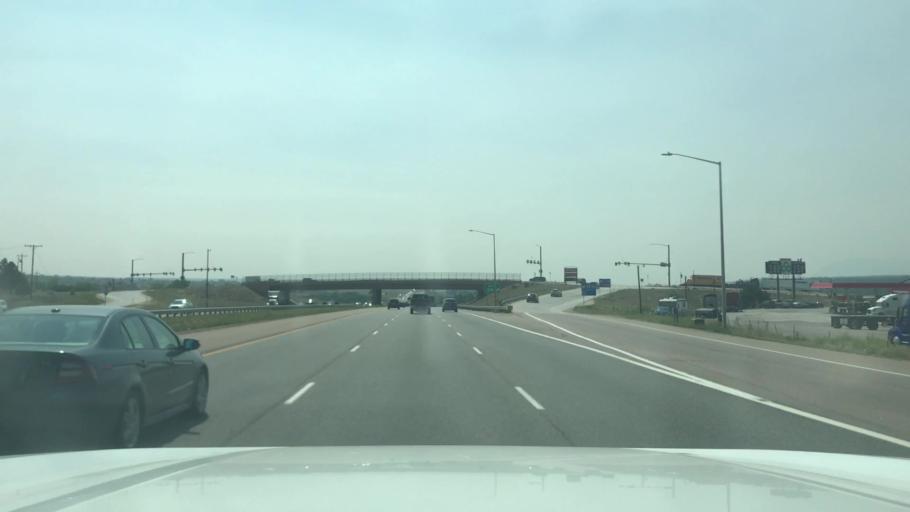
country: US
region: Colorado
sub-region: El Paso County
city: Gleneagle
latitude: 39.0590
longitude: -104.8530
